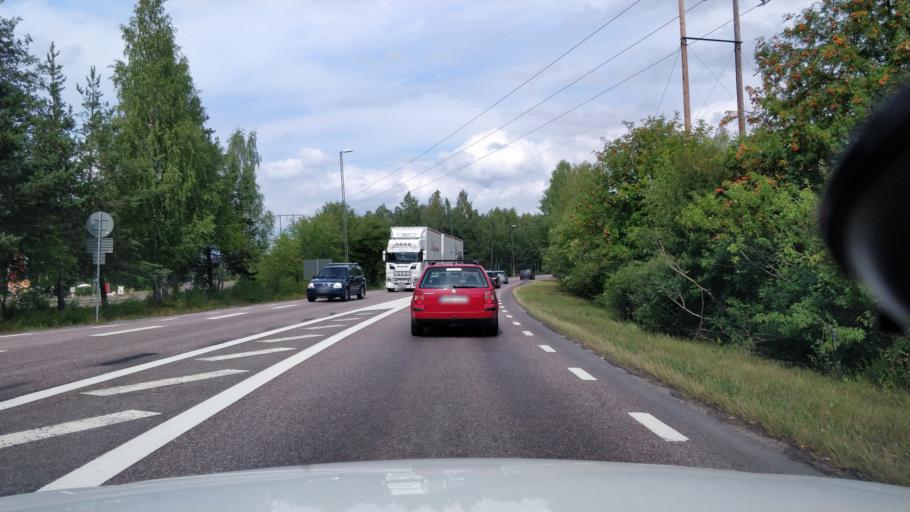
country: SE
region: Dalarna
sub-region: Faluns Kommun
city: Falun
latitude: 60.6177
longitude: 15.6130
